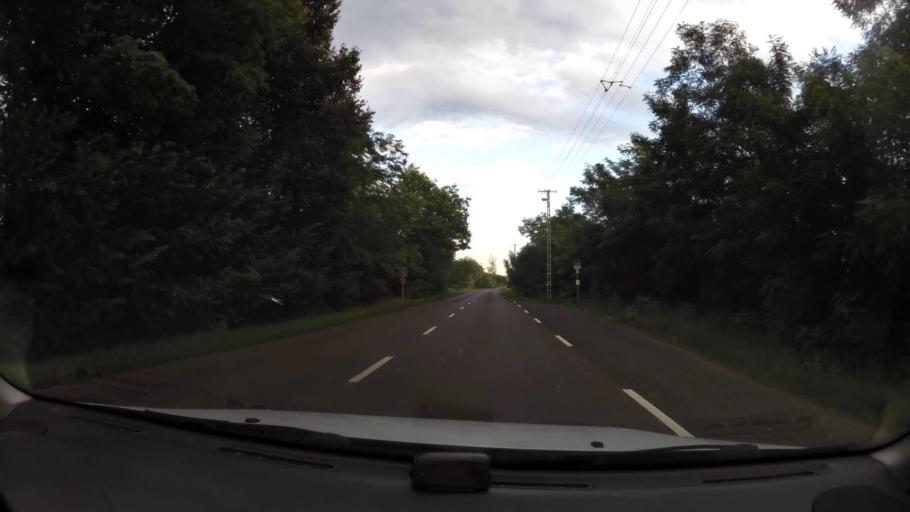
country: HU
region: Pest
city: Tapiobicske
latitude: 47.3754
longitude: 19.6704
